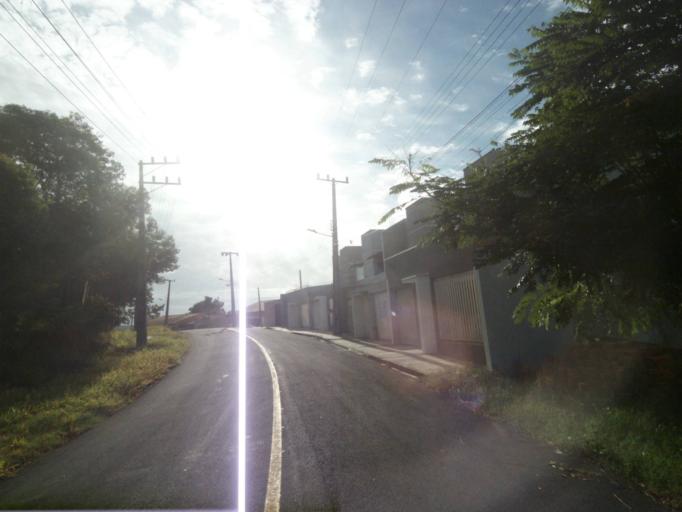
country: BR
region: Parana
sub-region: Telemaco Borba
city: Telemaco Borba
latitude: -24.3437
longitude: -50.6187
